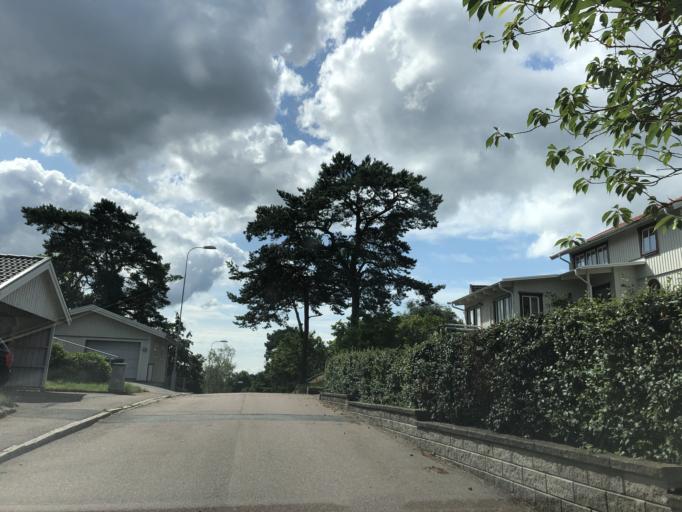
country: SE
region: Vaestra Goetaland
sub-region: Goteborg
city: Majorna
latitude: 57.7251
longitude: 11.9069
